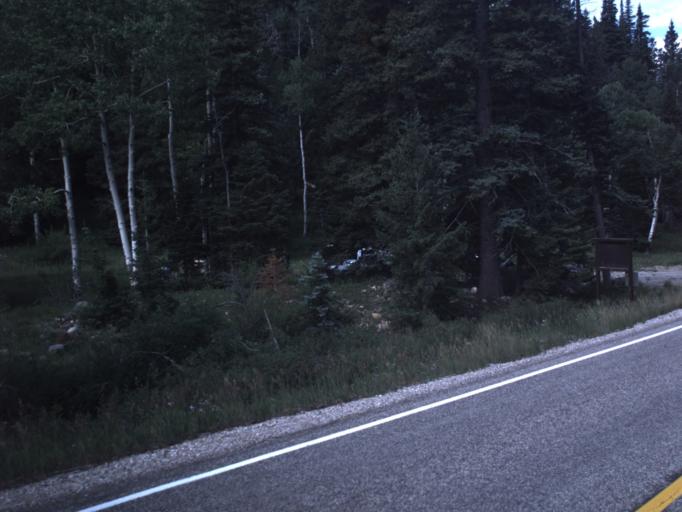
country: US
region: Utah
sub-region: Iron County
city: Cedar City
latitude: 37.5932
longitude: -112.9090
